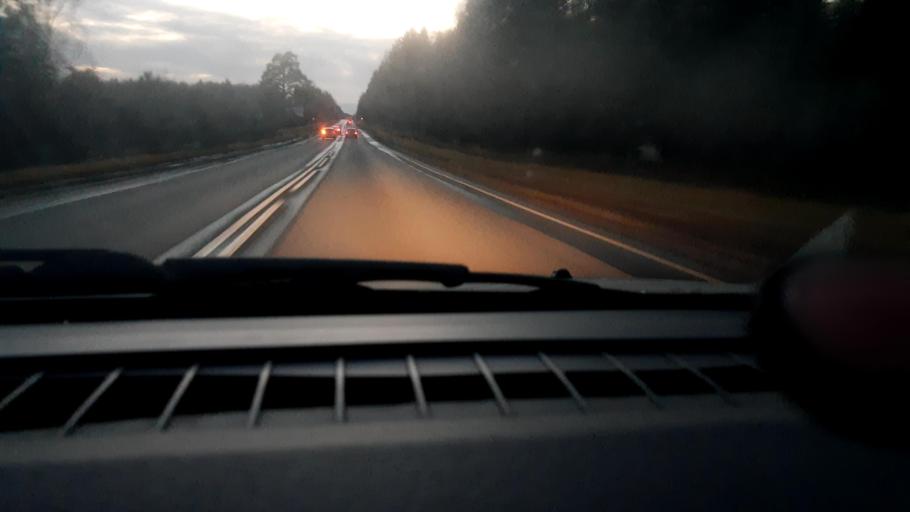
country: RU
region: Nizjnij Novgorod
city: Vladimirskoye
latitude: 56.8819
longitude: 44.9736
